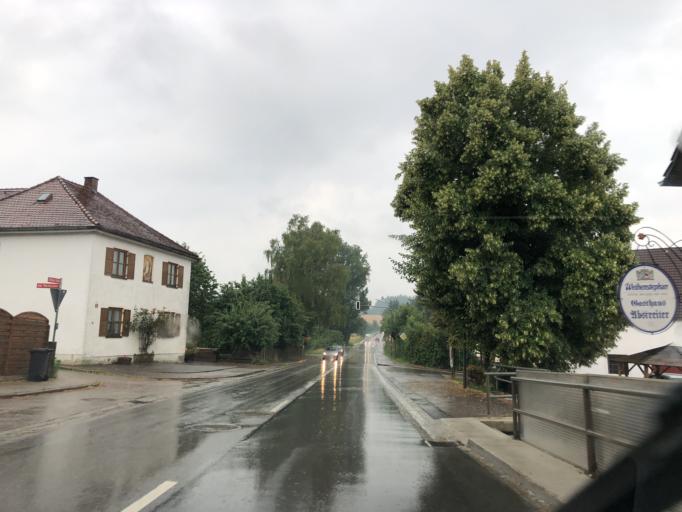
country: DE
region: Bavaria
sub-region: Upper Bavaria
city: Zolling
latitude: 48.4290
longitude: 11.7523
